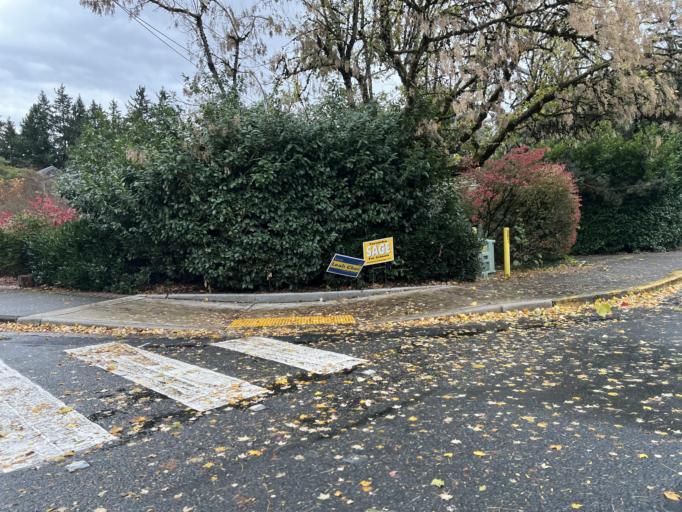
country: US
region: Washington
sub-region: King County
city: Redmond
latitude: 47.6748
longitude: -122.1152
